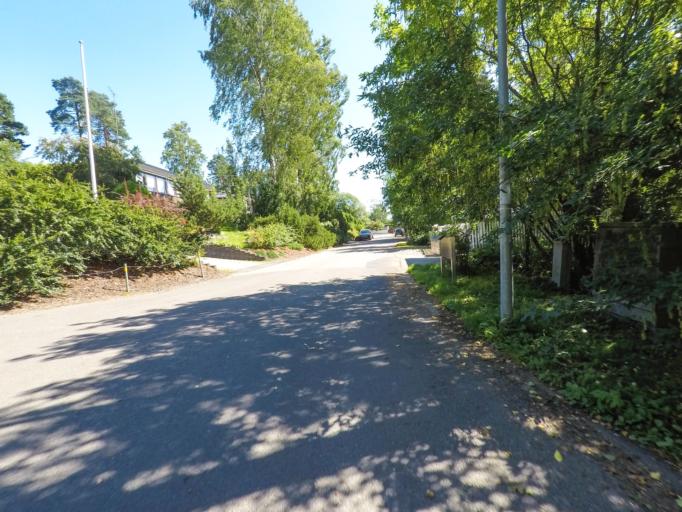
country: FI
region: Uusimaa
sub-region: Helsinki
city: Vantaa
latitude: 60.2017
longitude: 25.0906
